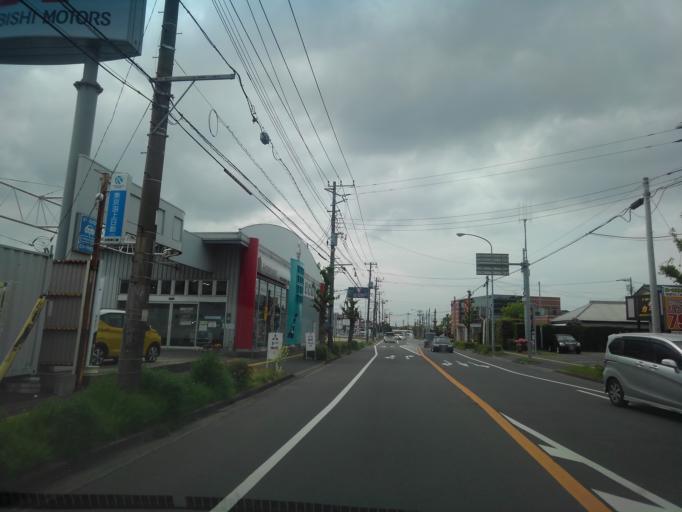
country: JP
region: Chiba
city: Kimitsu
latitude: 35.3293
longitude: 139.9231
